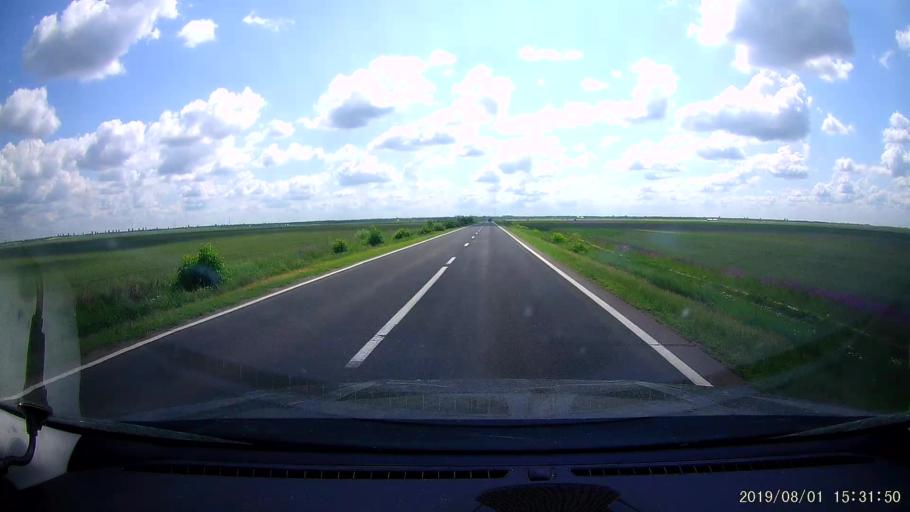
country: RO
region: Braila
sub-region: Comuna Insuratei
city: Insuratei
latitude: 44.9398
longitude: 27.6511
